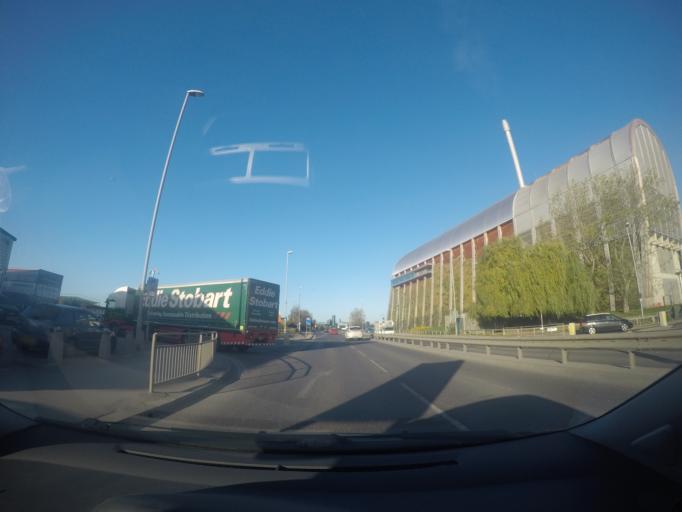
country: GB
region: England
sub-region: City and Borough of Leeds
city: Leeds
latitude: 53.7867
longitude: -1.5025
